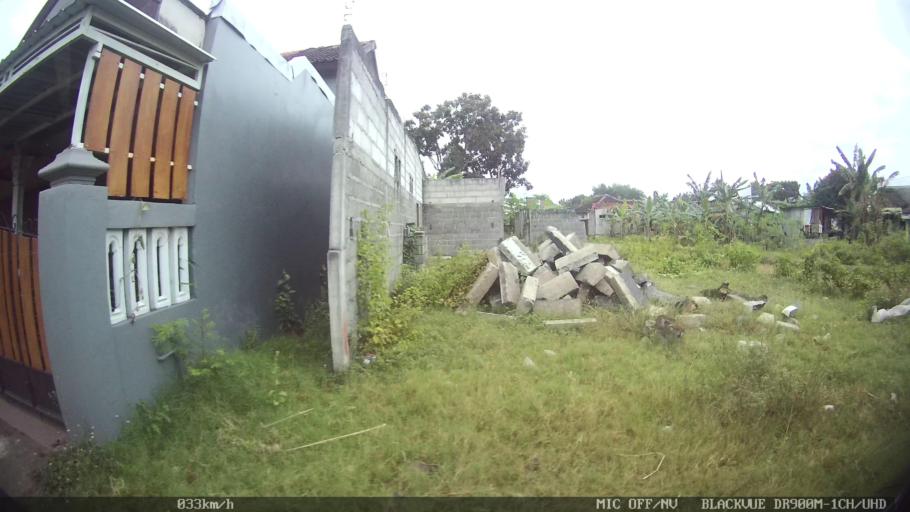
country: ID
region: Daerah Istimewa Yogyakarta
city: Sewon
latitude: -7.8527
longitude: 110.3968
